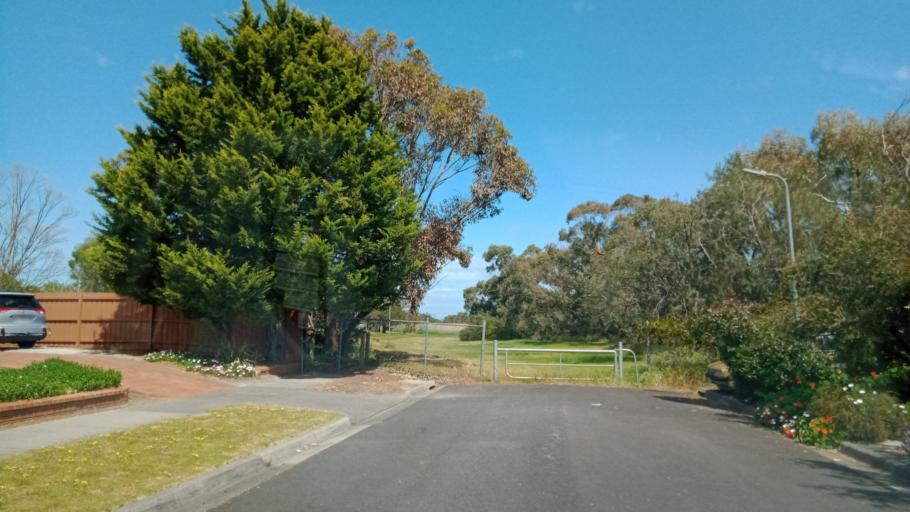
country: AU
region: Victoria
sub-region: Kingston
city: Chelsea Heights
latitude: -38.0347
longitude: 145.1314
